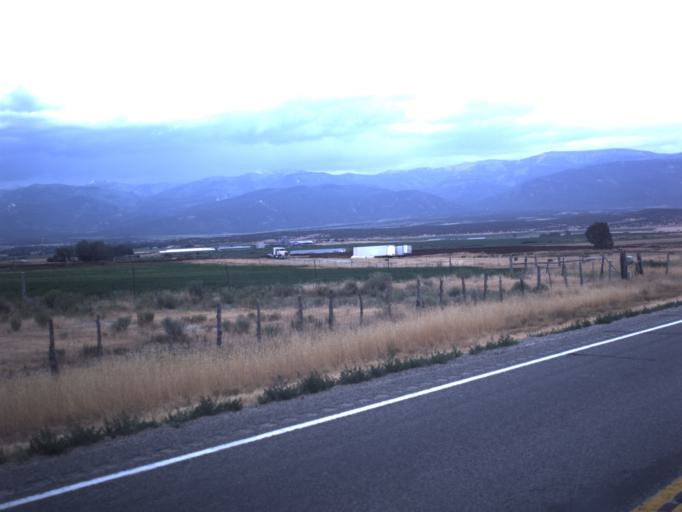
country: US
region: Utah
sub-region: Sanpete County
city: Moroni
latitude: 39.4955
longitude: -111.5637
